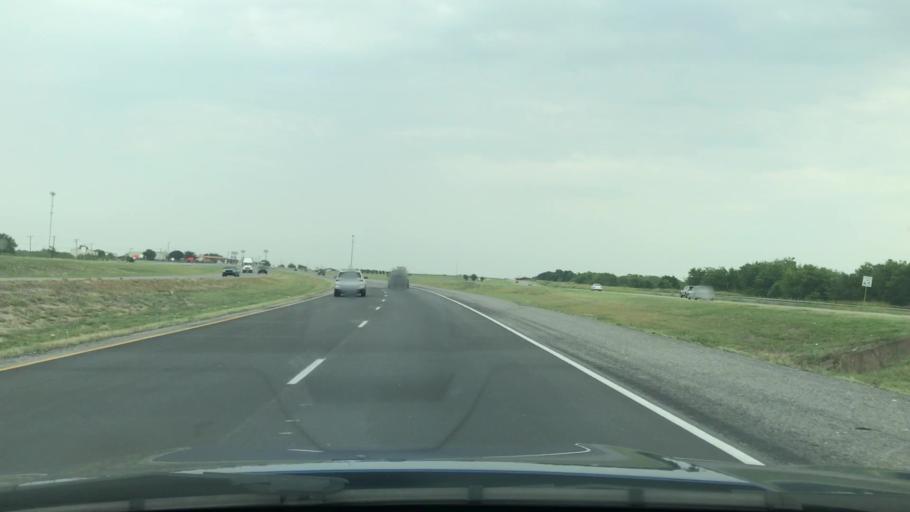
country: US
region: Texas
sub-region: Kaufman County
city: Talty
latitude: 32.7392
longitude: -96.3700
